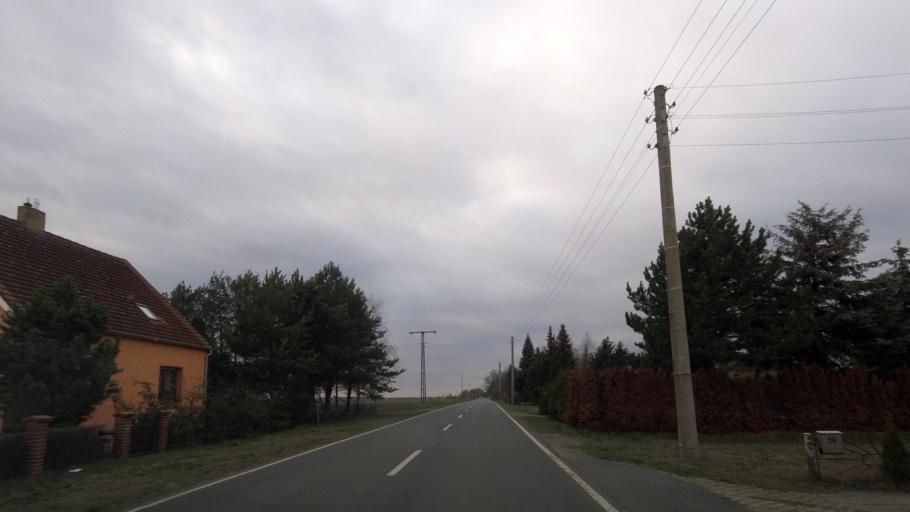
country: DE
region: Saxony-Anhalt
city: Kemberg
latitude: 51.7818
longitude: 12.6222
